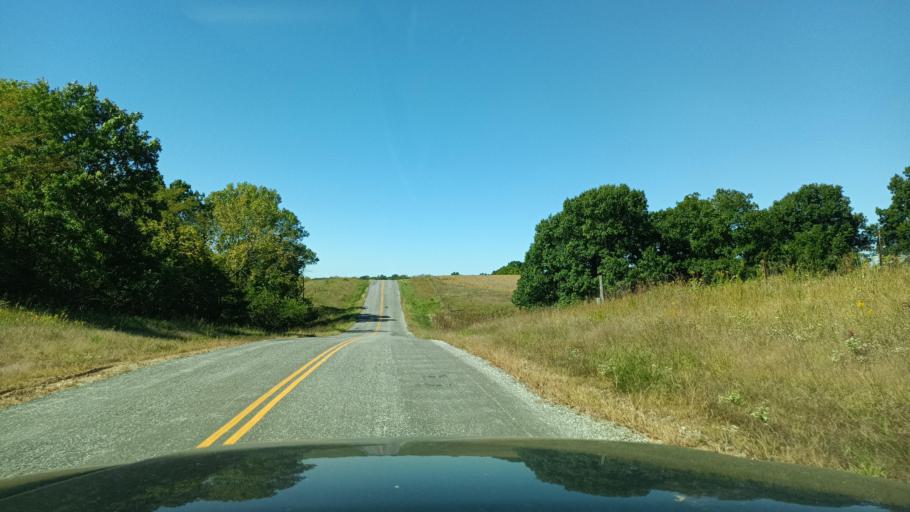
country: US
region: Missouri
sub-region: Adair County
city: Kirksville
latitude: 40.3301
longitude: -92.5404
